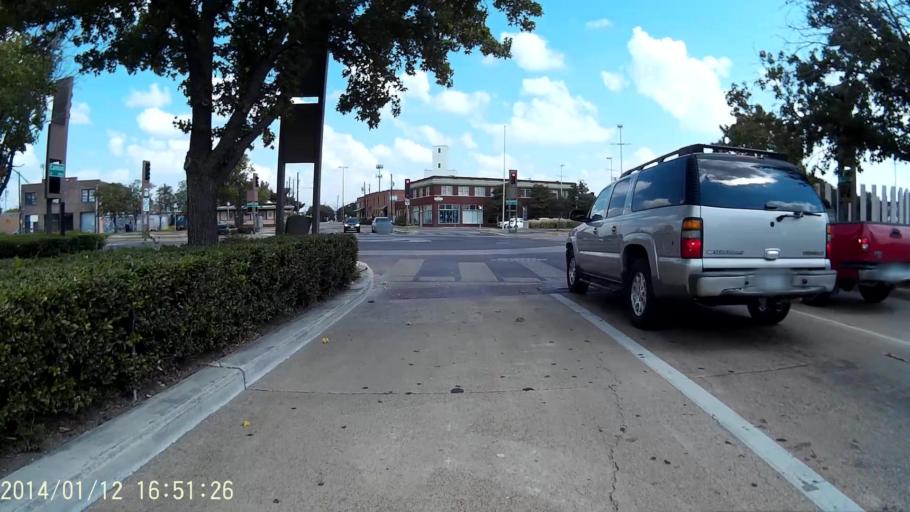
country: US
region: Texas
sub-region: Dallas County
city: Dallas
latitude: 32.7843
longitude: -96.7740
